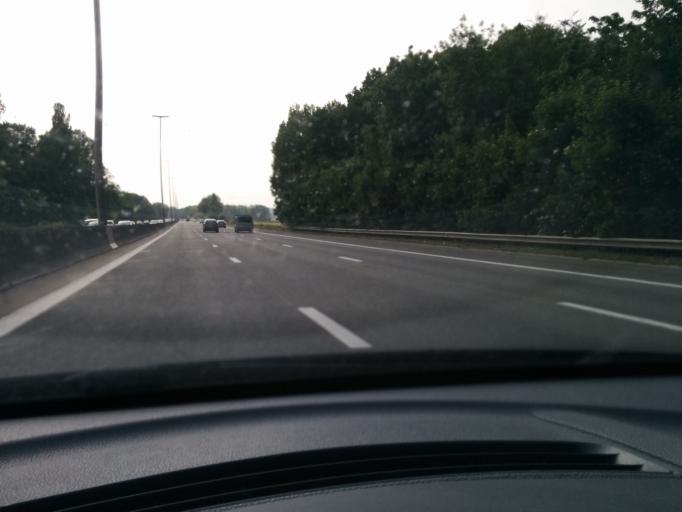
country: BE
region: Flanders
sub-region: Provincie Vlaams-Brabant
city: Dilbeek
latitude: 50.8823
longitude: 4.2376
